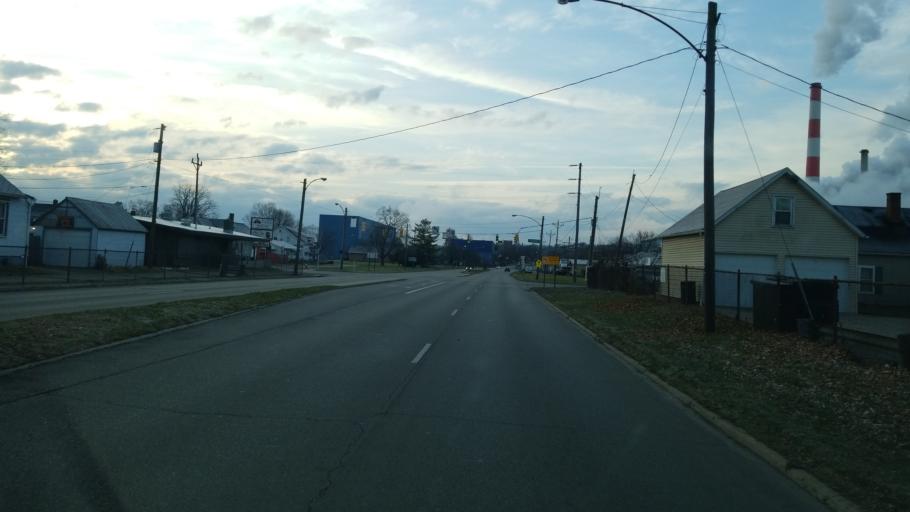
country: US
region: Ohio
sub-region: Ross County
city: Chillicothe
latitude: 39.3307
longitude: -82.9733
